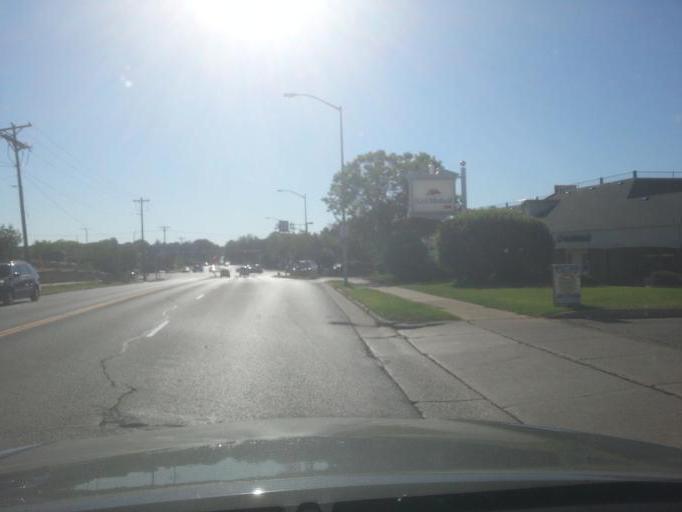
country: US
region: Wisconsin
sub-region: Dane County
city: Shorewood Hills
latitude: 43.0500
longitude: -89.4753
